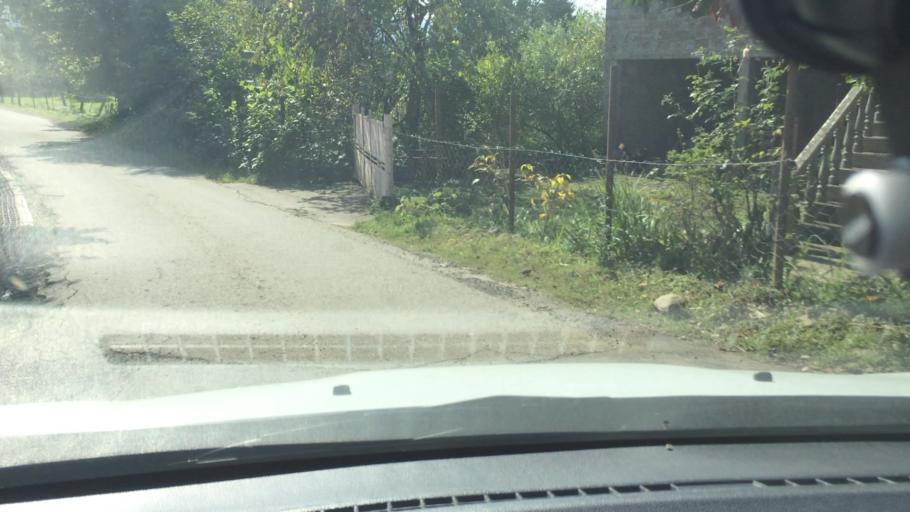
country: GE
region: Ajaria
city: Kobuleti
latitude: 41.8116
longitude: 41.8243
